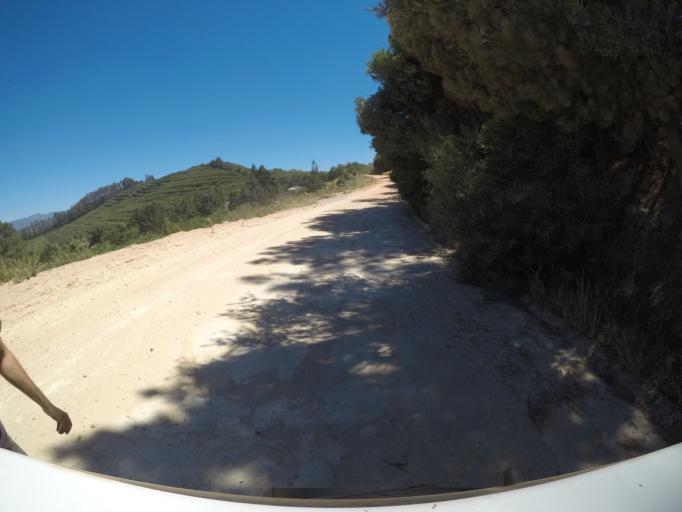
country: ZA
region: Western Cape
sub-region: Overberg District Municipality
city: Grabouw
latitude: -34.2418
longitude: 19.0863
